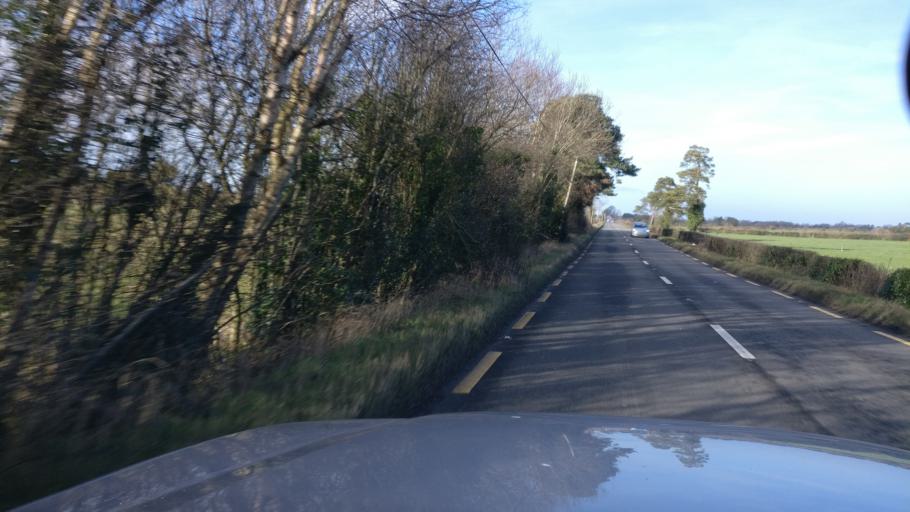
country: IE
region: Leinster
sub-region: Laois
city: Mountmellick
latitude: 53.0884
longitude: -7.3343
